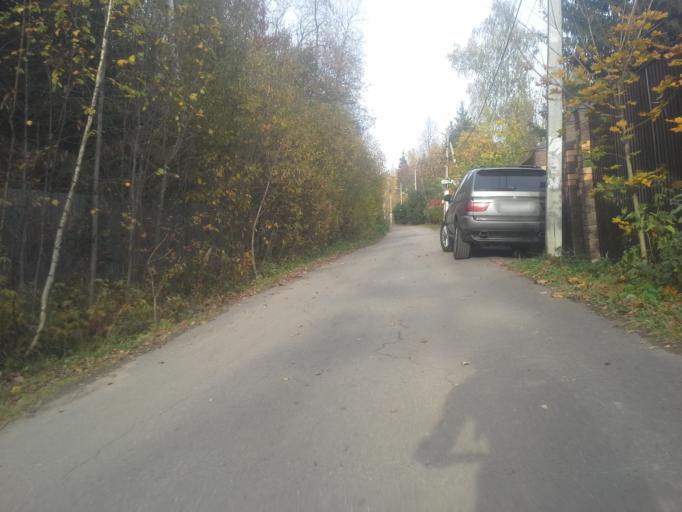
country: RU
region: Moskovskaya
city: Krasnoznamensk
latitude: 55.5752
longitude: 37.0150
